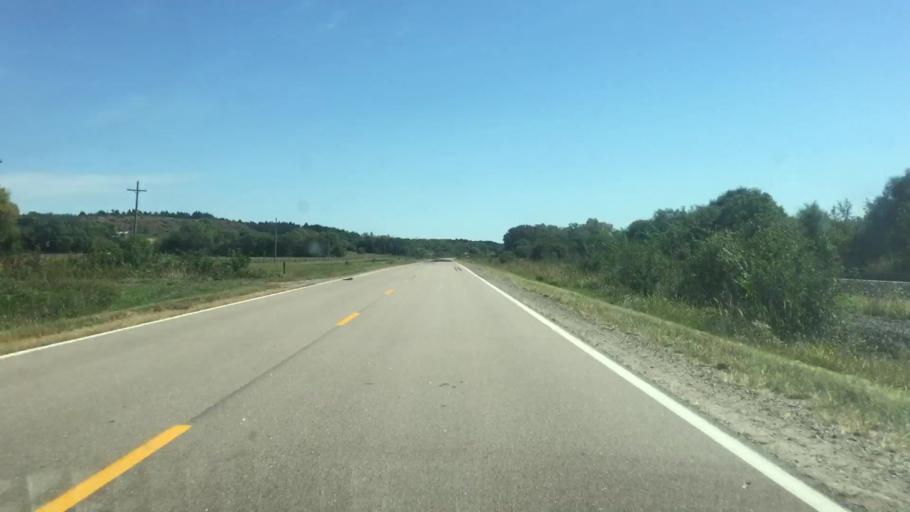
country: US
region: Nebraska
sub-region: Jefferson County
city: Fairbury
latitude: 40.0760
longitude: -97.0808
